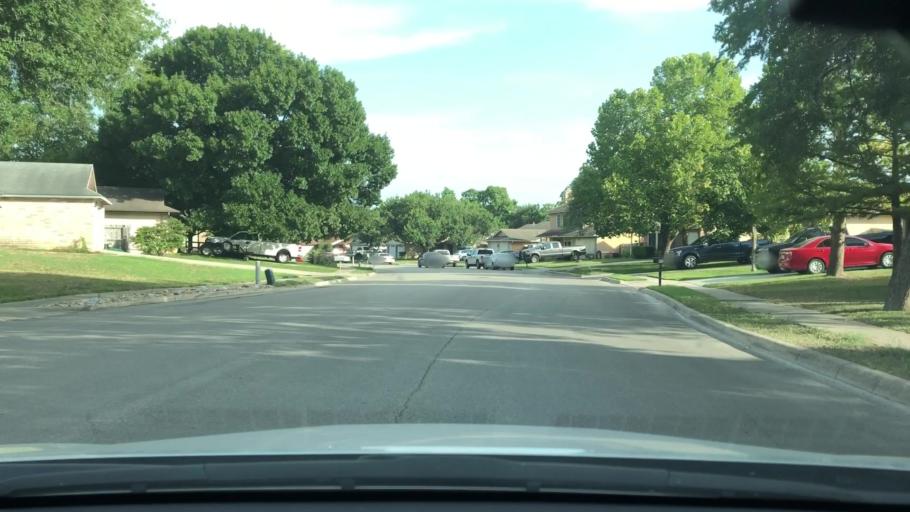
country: US
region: Texas
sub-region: Bexar County
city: Converse
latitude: 29.5380
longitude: -98.3266
